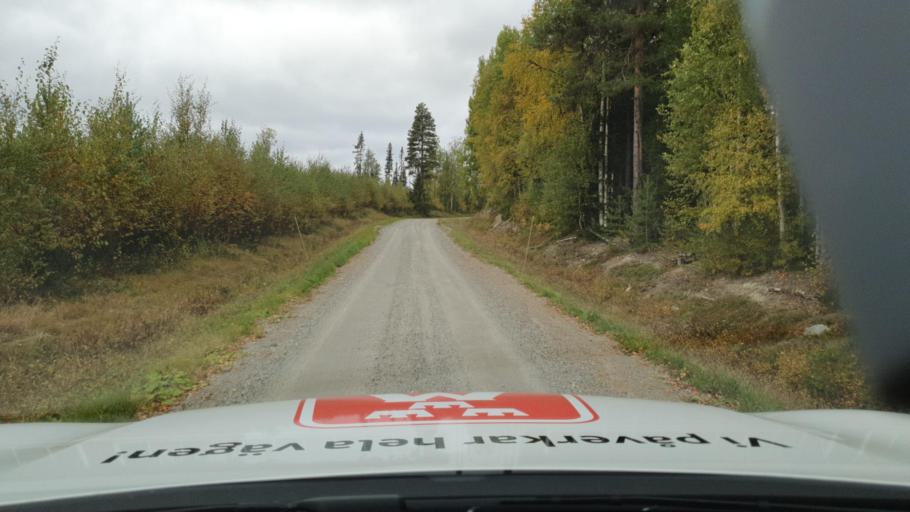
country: SE
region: Vaesterbotten
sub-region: Asele Kommun
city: Asele
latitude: 64.1488
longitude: 16.9459
